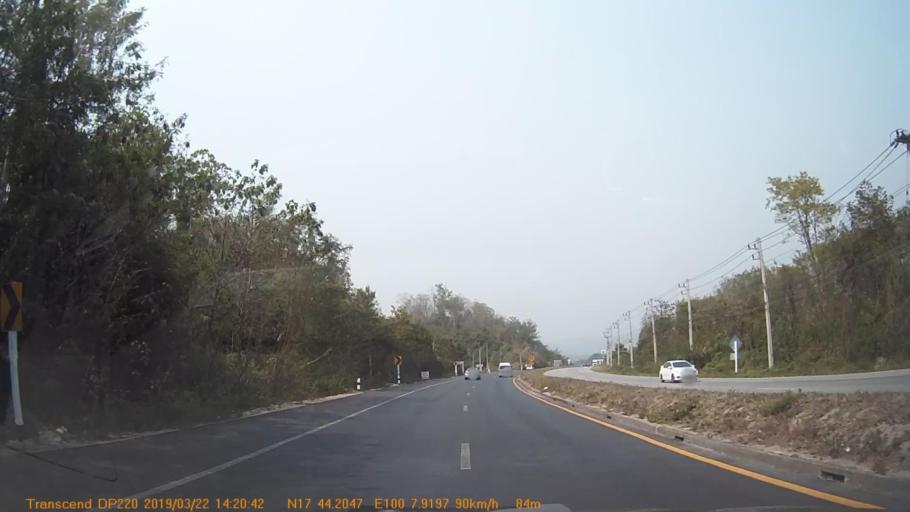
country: TH
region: Uttaradit
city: Uttaradit
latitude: 17.7372
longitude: 100.1320
